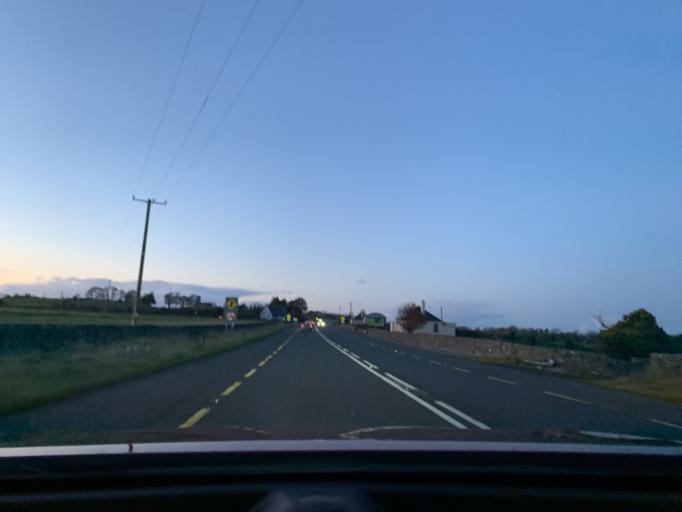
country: IE
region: Connaught
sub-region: Roscommon
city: Boyle
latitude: 53.9641
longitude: -8.1958
